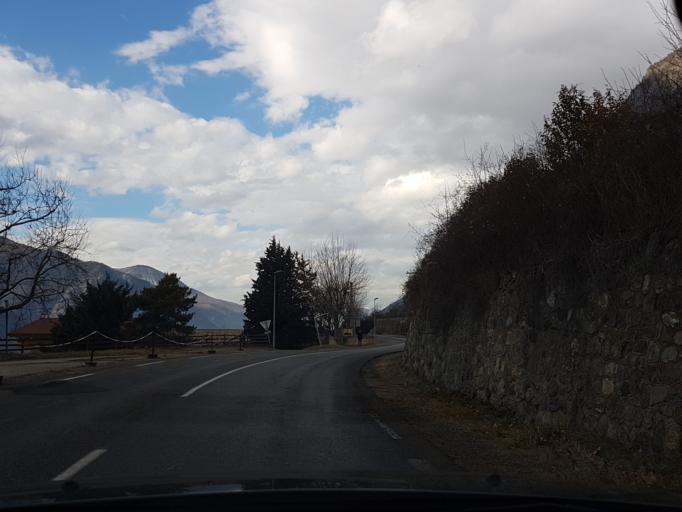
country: FR
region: Provence-Alpes-Cote d'Azur
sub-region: Departement des Hautes-Alpes
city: La Batie-Neuve
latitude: 44.4673
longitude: 6.1635
